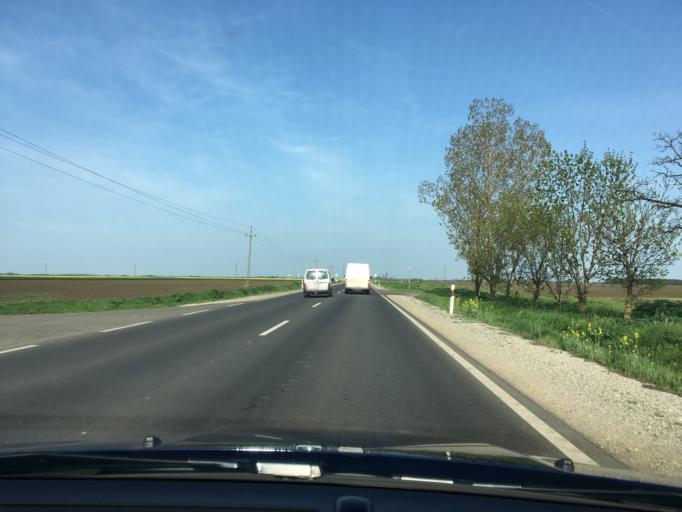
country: HU
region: Bekes
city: Ujkigyos
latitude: 46.6643
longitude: 20.9617
